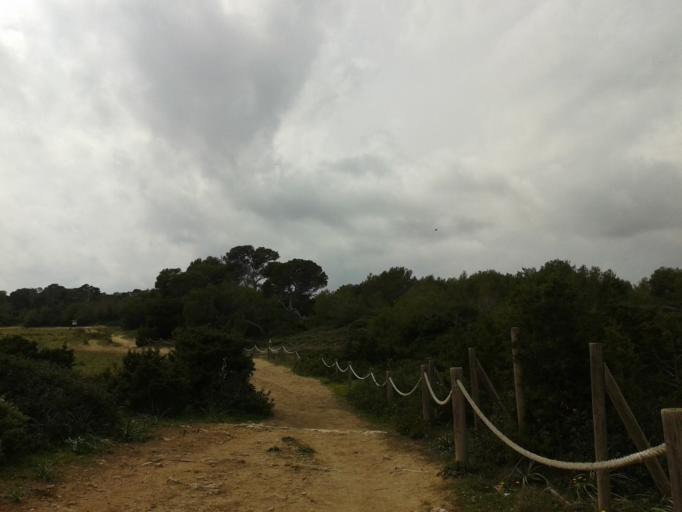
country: ES
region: Balearic Islands
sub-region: Illes Balears
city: Son Servera
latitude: 39.5847
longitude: 3.3912
